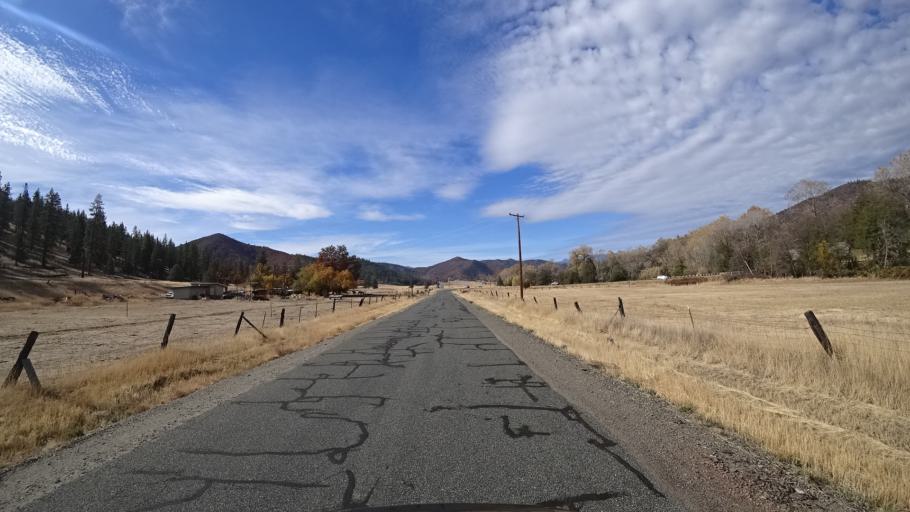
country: US
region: California
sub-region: Siskiyou County
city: Yreka
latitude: 41.6327
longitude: -122.7510
